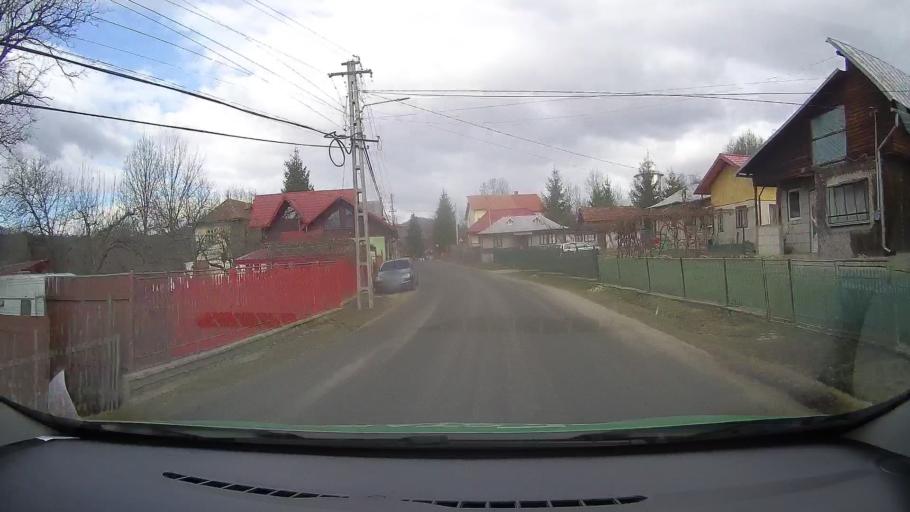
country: RO
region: Prahova
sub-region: Comuna Provita de Sus
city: Provita de Sus
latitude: 45.1345
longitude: 25.6399
